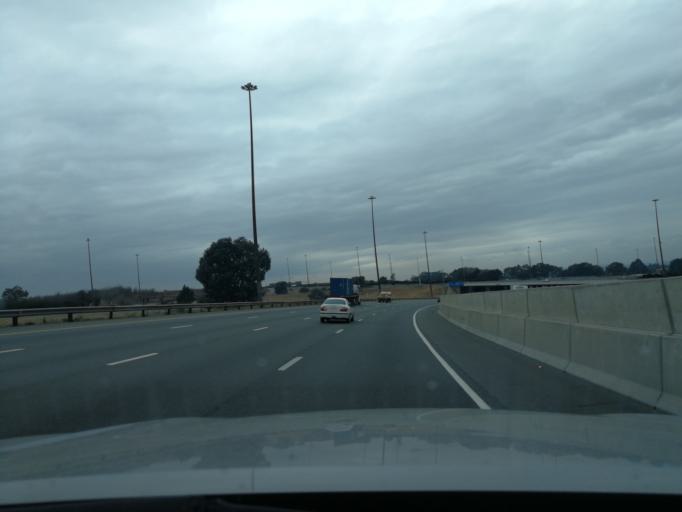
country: ZA
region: Gauteng
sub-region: Ekurhuleni Metropolitan Municipality
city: Germiston
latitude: -26.2489
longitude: 28.1454
